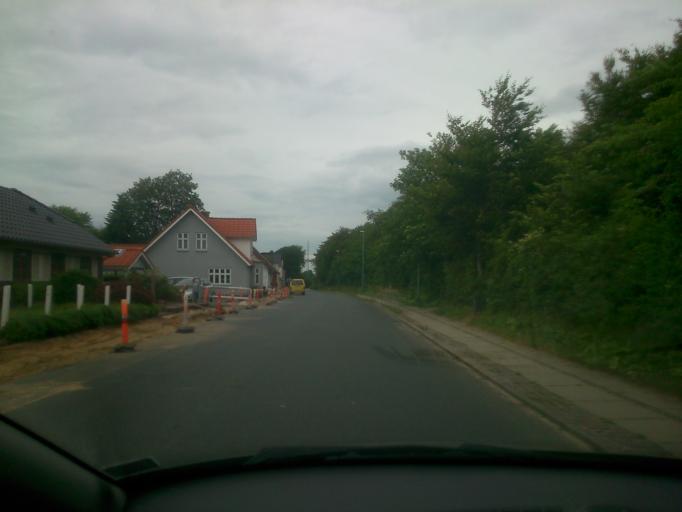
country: DK
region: South Denmark
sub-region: Esbjerg Kommune
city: Esbjerg
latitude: 55.5335
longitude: 8.4413
